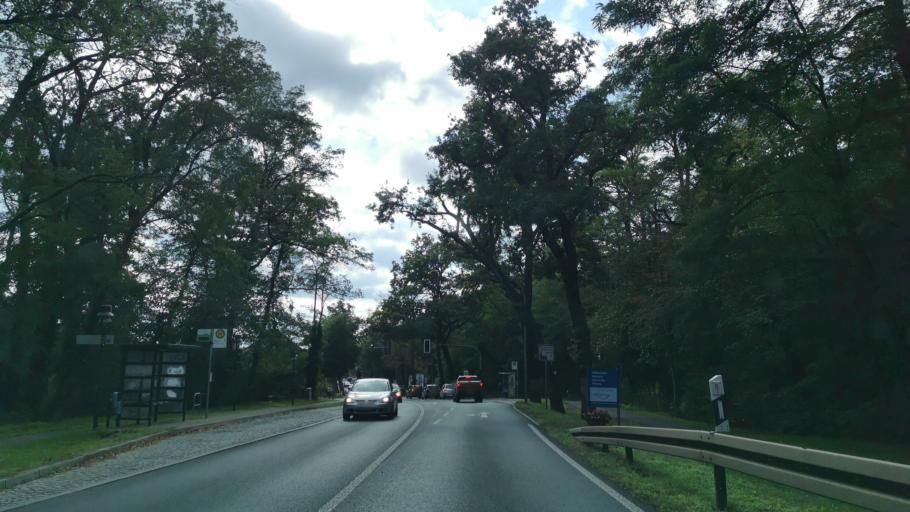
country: DE
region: Brandenburg
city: Werder
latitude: 52.3656
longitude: 12.9867
